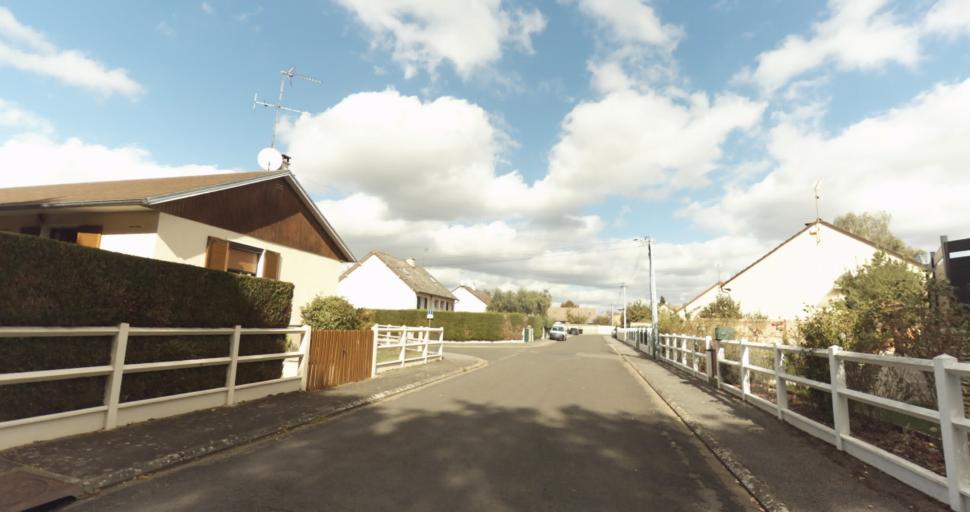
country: FR
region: Centre
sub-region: Departement d'Eure-et-Loir
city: Garnay
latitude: 48.7237
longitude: 1.3234
